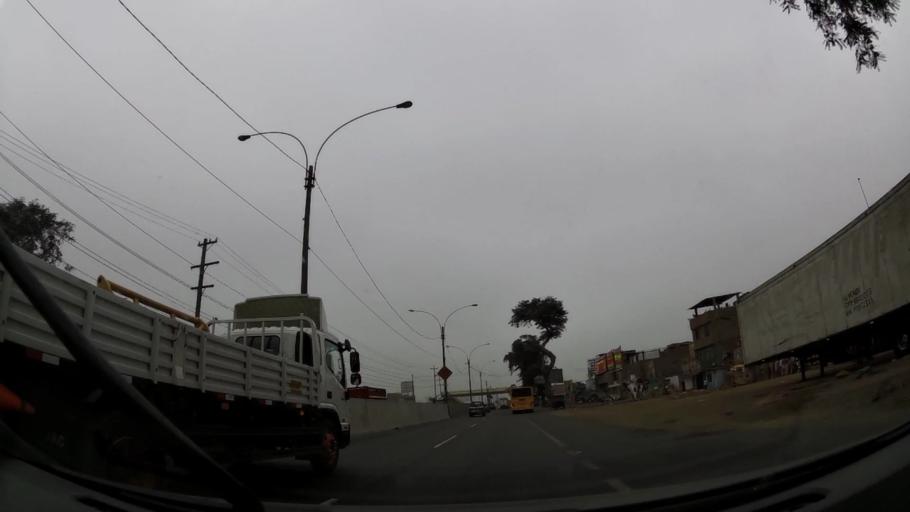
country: PE
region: Lima
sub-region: Lima
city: Urb. Santo Domingo
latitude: -11.8834
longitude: -77.0687
